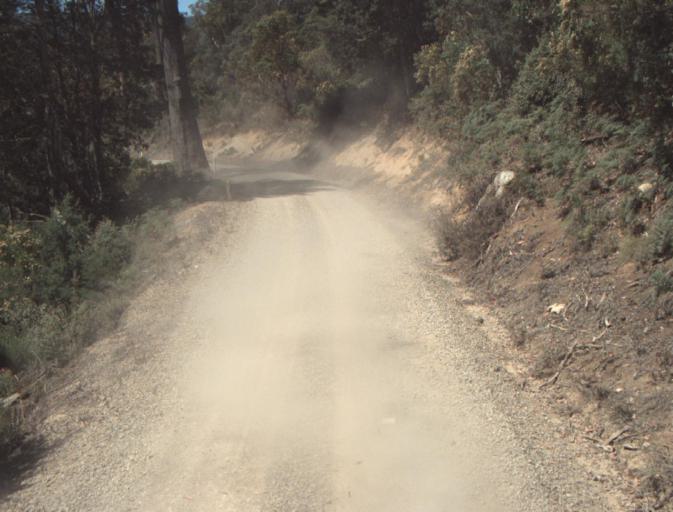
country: AU
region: Tasmania
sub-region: Dorset
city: Scottsdale
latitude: -41.3184
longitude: 147.4620
